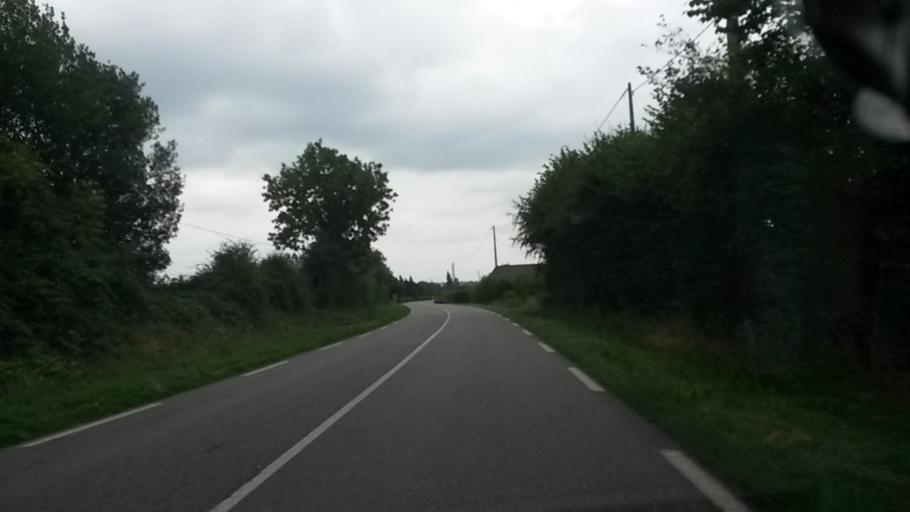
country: FR
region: Haute-Normandie
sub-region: Departement de la Seine-Maritime
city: Forges-les-Eaux
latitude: 49.6261
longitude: 1.5722
